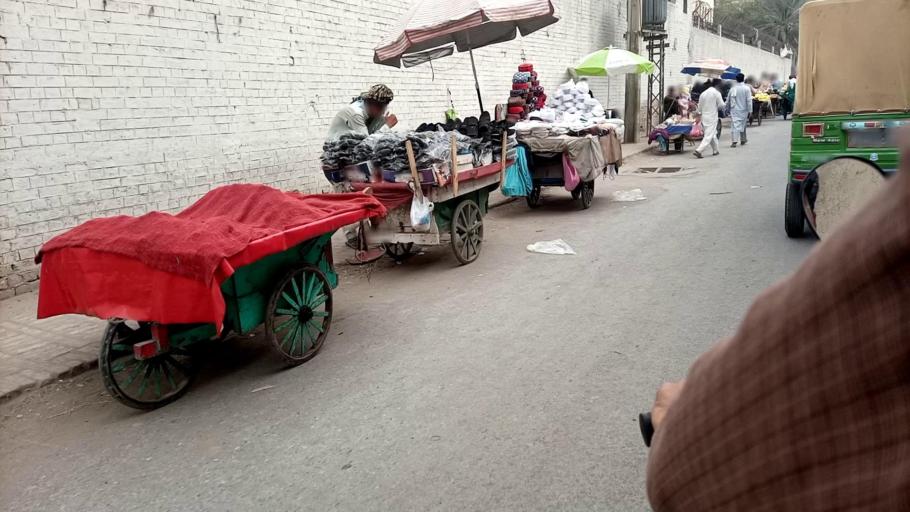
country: PK
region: Khyber Pakhtunkhwa
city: Peshawar
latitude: 34.0161
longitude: 71.5803
